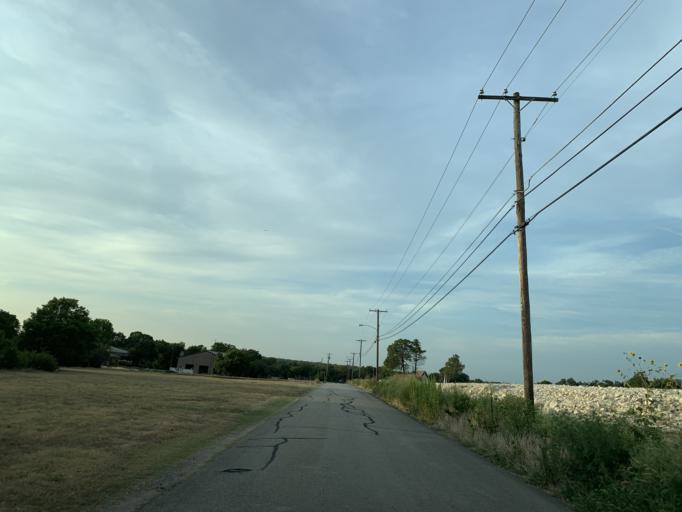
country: US
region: Texas
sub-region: Dallas County
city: Cockrell Hill
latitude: 32.7030
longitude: -96.8829
